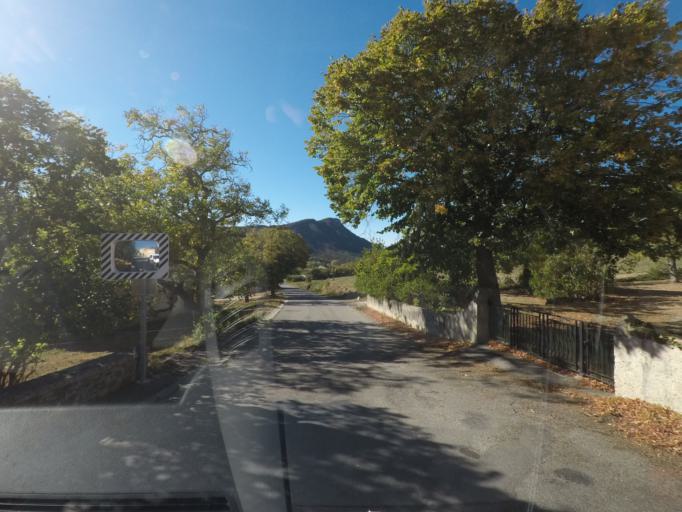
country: FR
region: Provence-Alpes-Cote d'Azur
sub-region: Departement des Hautes-Alpes
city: Serres
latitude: 44.4510
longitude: 5.5402
